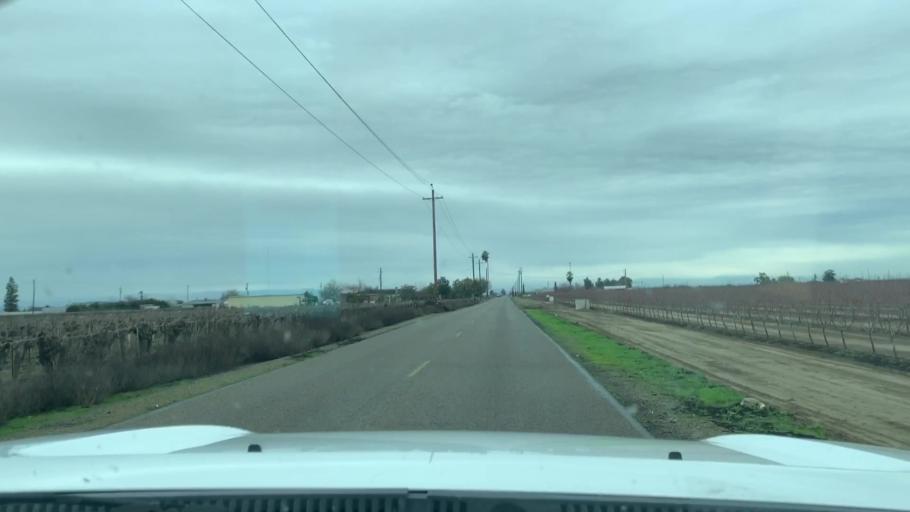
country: US
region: California
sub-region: Fresno County
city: Caruthers
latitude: 36.5474
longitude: -119.7772
